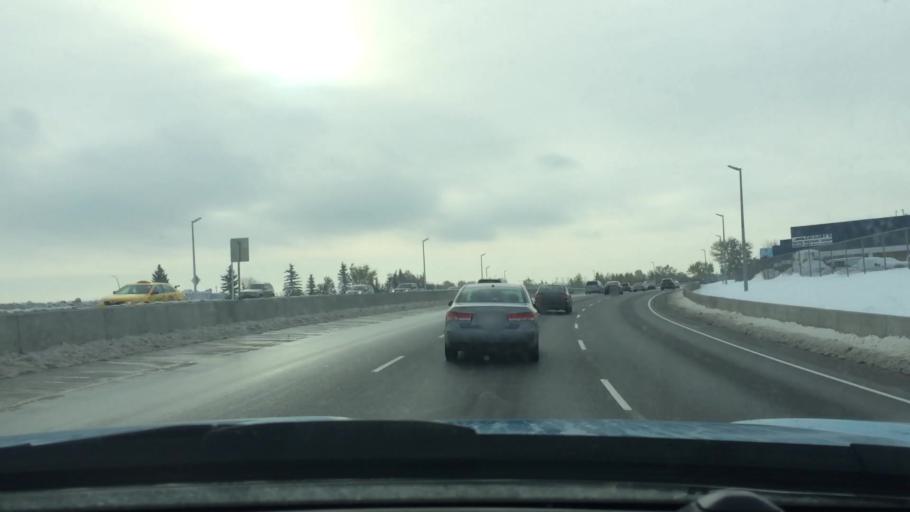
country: CA
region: Alberta
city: Calgary
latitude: 51.0952
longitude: -114.0278
